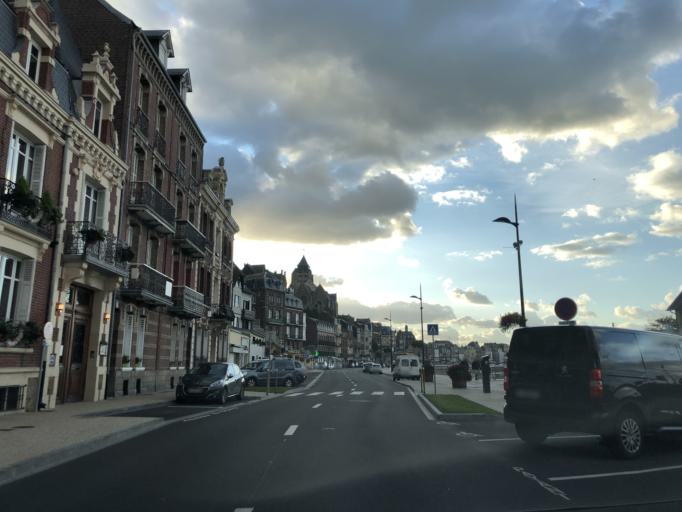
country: FR
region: Haute-Normandie
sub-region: Departement de la Seine-Maritime
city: Le Treport
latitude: 50.0598
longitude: 1.3777
